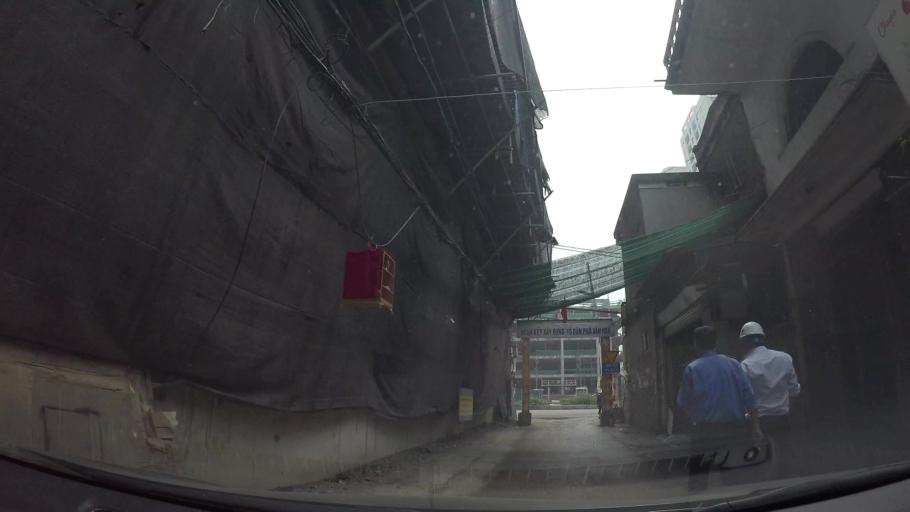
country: VN
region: Ha Noi
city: Van Dien
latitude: 20.9680
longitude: 105.8673
